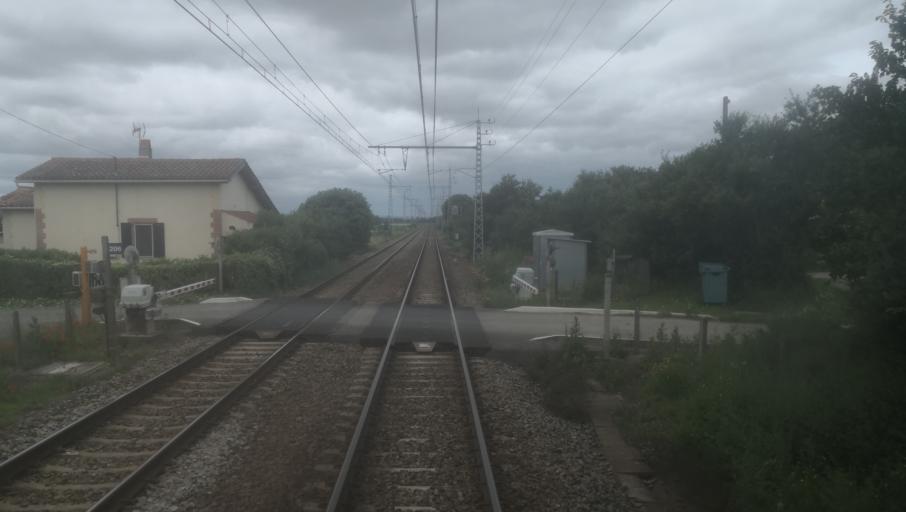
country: FR
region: Midi-Pyrenees
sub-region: Departement de la Haute-Garonne
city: Villenouvelle
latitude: 43.4373
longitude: 1.6516
